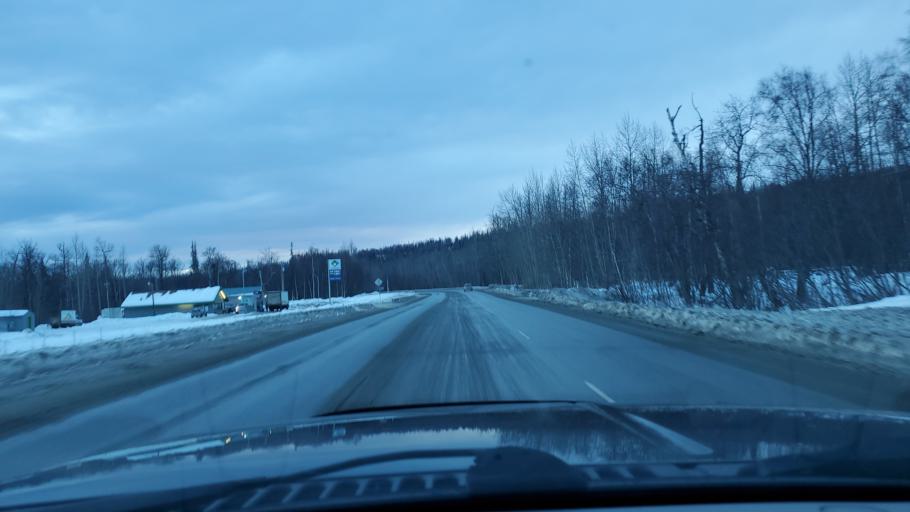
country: US
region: Alaska
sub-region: Matanuska-Susitna Borough
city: Lazy Mountain
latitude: 61.7089
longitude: -148.9330
